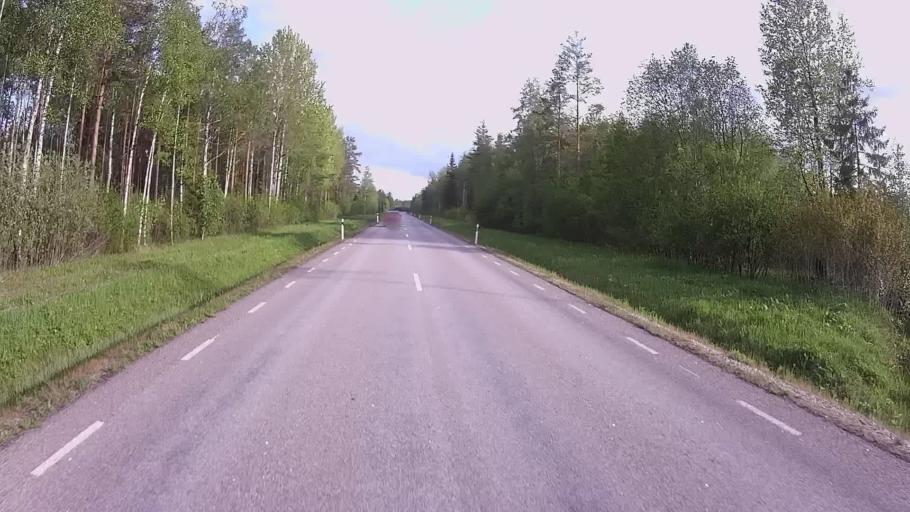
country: EE
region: Jogevamaa
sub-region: Mustvee linn
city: Mustvee
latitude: 59.0694
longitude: 26.9993
